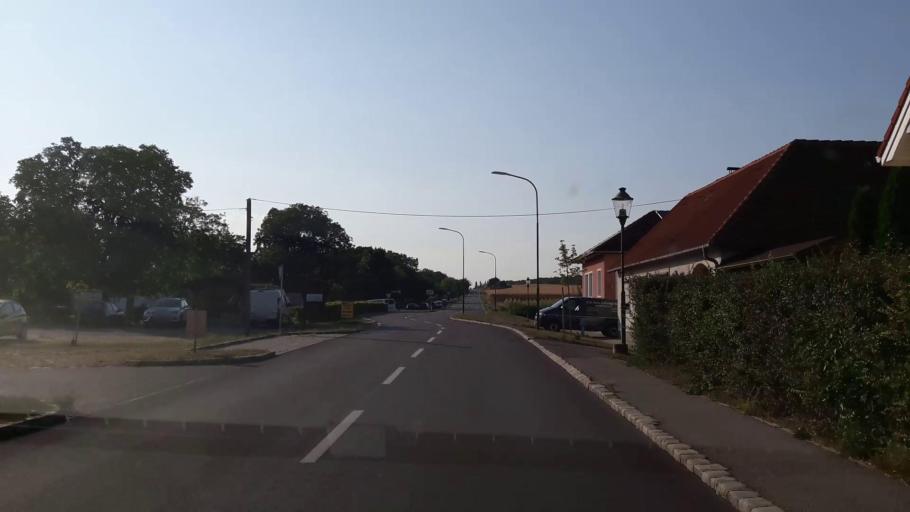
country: AT
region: Lower Austria
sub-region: Politischer Bezirk Ganserndorf
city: Orth an der Donau
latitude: 48.0689
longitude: 16.7022
